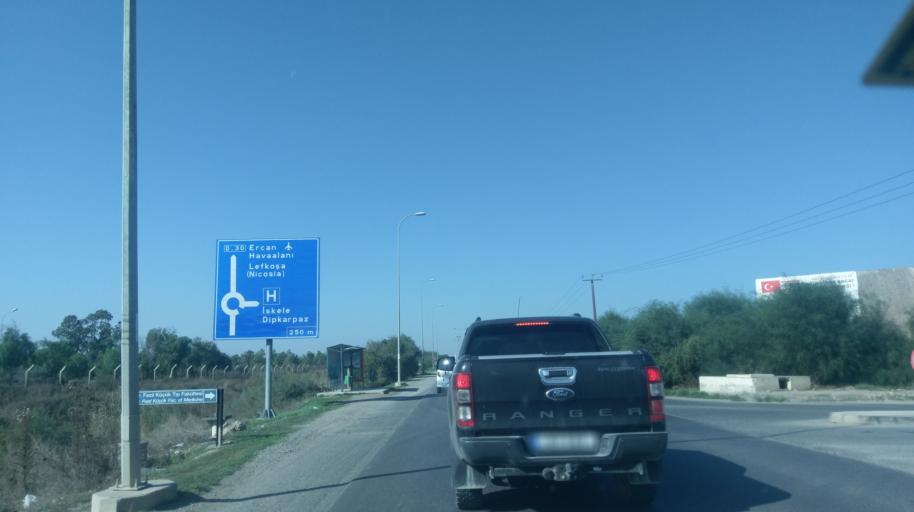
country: CY
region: Ammochostos
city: Famagusta
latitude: 35.1435
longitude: 33.8985
